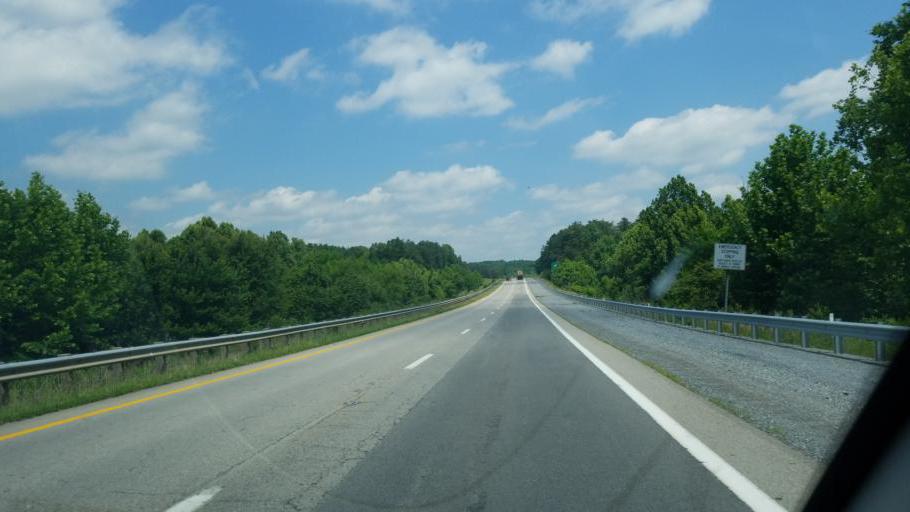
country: US
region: Virginia
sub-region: Pittsylvania County
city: Motley
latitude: 37.0956
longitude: -79.3319
